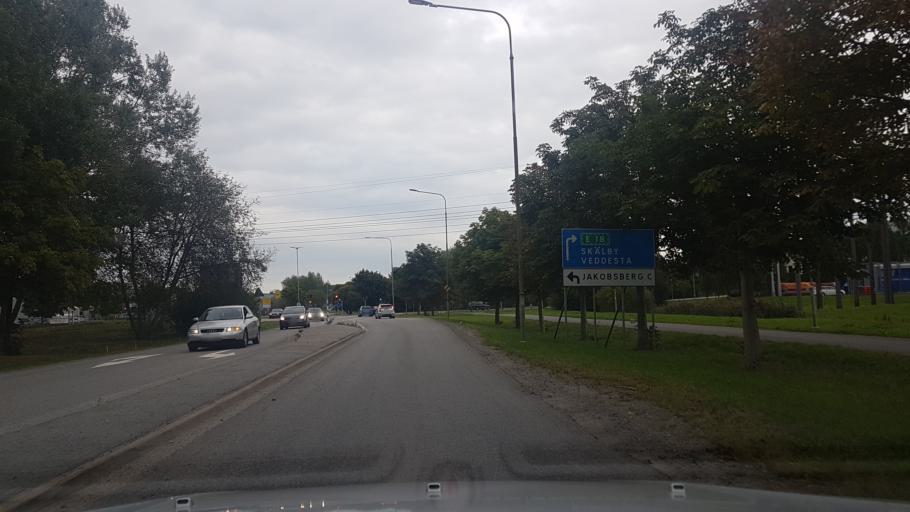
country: SE
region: Stockholm
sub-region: Jarfalla Kommun
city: Jakobsberg
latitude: 59.4153
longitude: 17.8265
